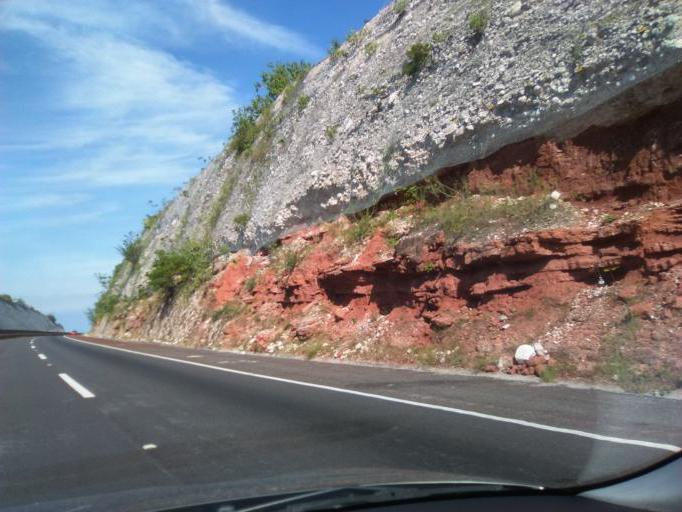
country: MX
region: Guerrero
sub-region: Huitzuco de los Figueroa
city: San Francisco Ozomatlan
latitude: 18.0396
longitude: -99.2644
